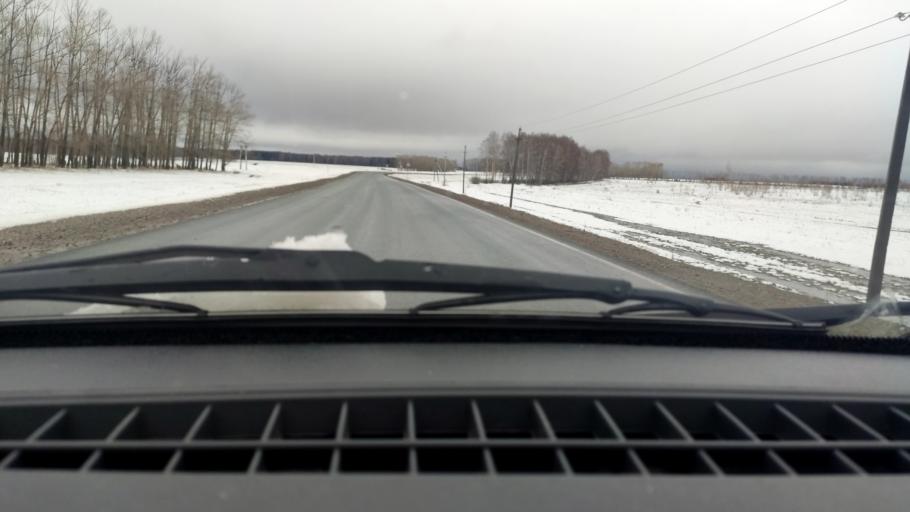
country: RU
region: Bashkortostan
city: Kushnarenkovo
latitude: 55.0569
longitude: 55.1566
